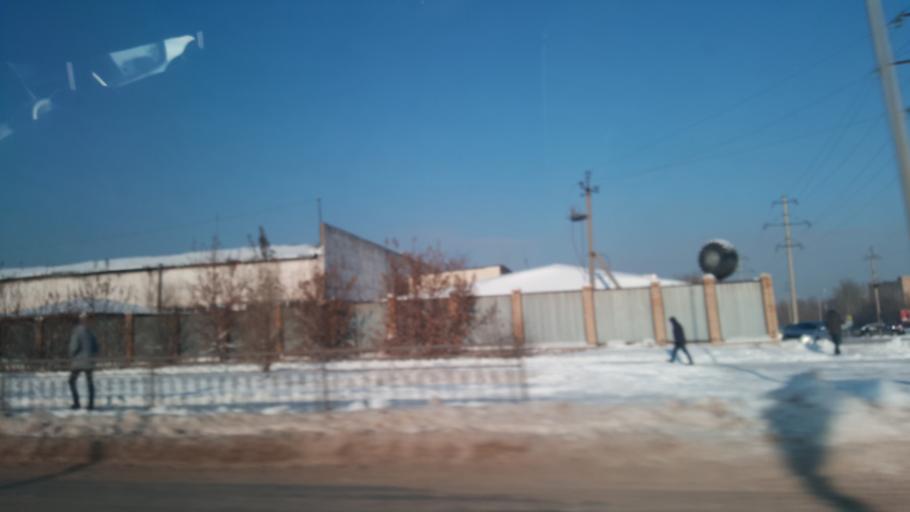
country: KZ
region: Astana Qalasy
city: Astana
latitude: 51.1789
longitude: 71.4685
